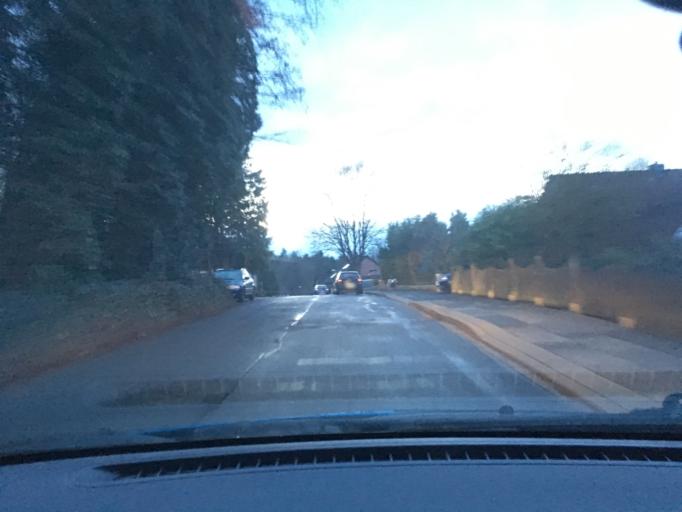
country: DE
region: Lower Saxony
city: Embsen
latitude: 53.1731
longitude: 10.3471
